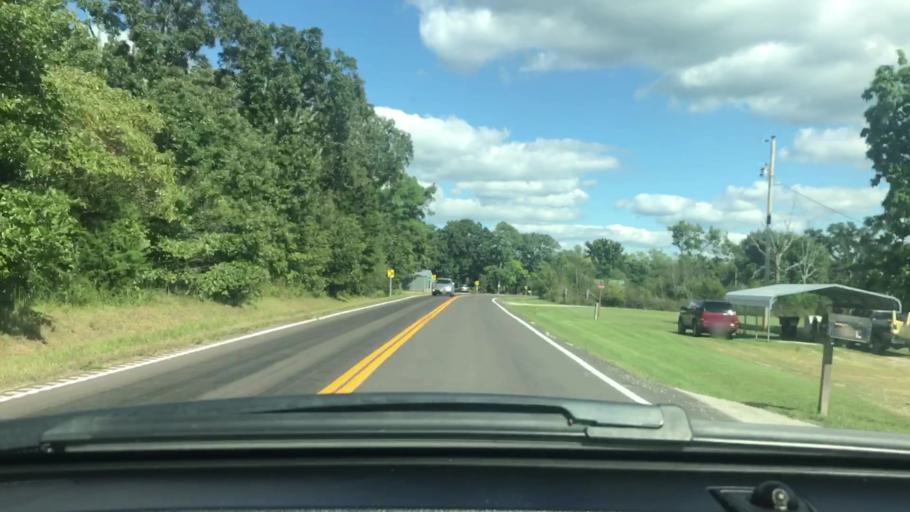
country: US
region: Missouri
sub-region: Wright County
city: Mountain Grove
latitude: 37.2544
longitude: -92.3044
